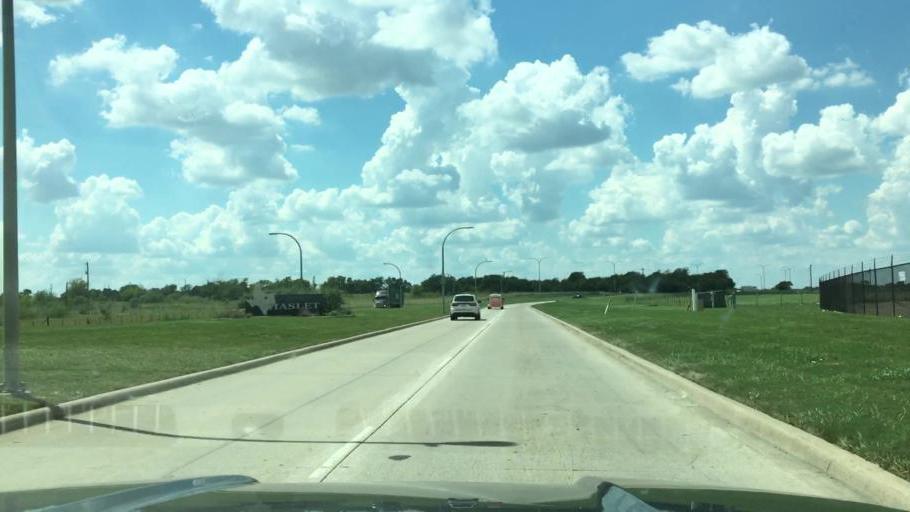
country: US
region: Texas
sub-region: Tarrant County
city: Haslet
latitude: 32.9724
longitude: -97.3164
